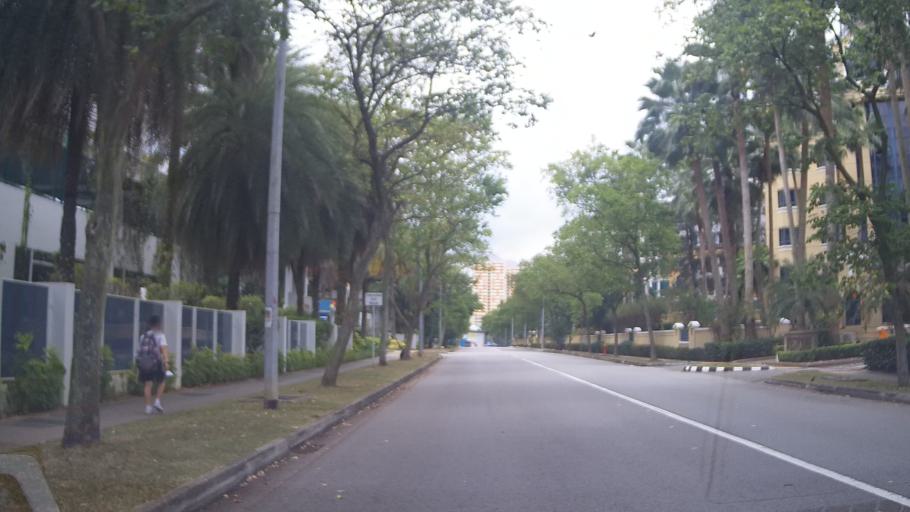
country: SG
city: Singapore
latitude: 1.2974
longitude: 103.7659
